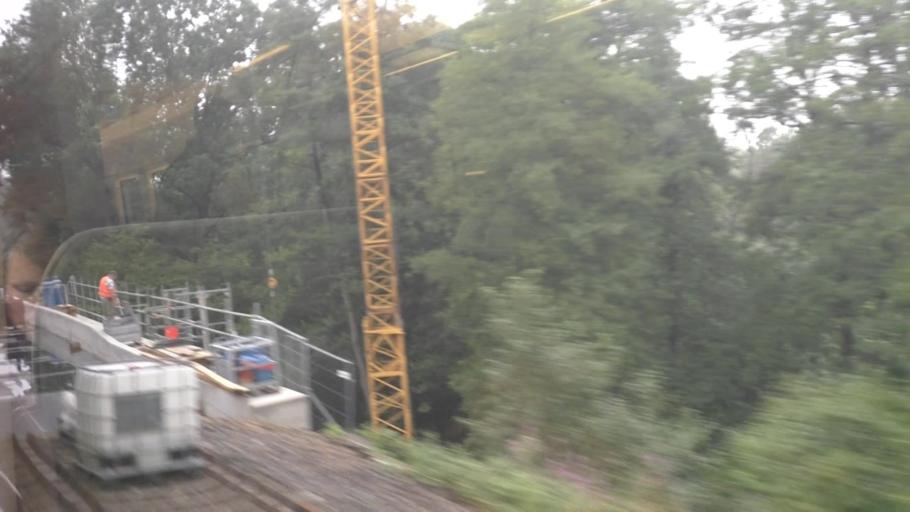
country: DE
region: Saxony
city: Radeberg
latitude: 51.1054
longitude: 13.9362
